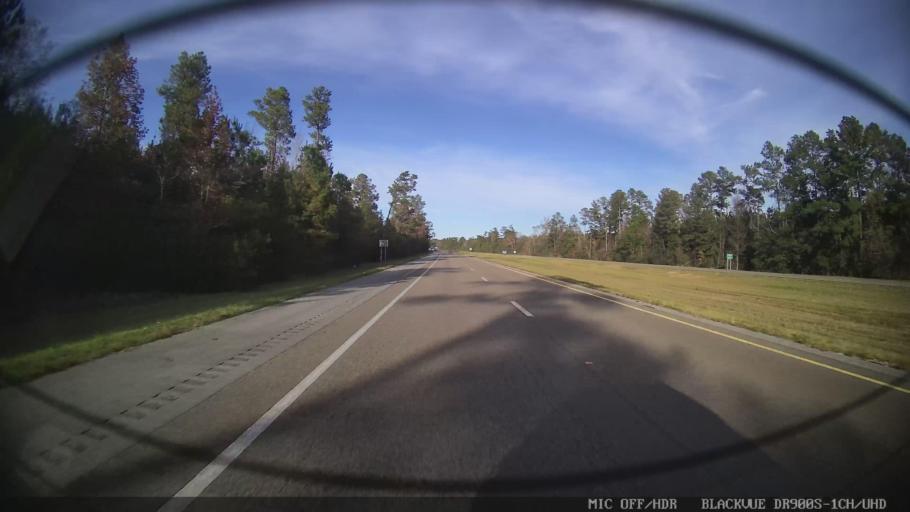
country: US
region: Mississippi
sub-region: Lamar County
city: Purvis
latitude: 31.1748
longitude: -89.3491
